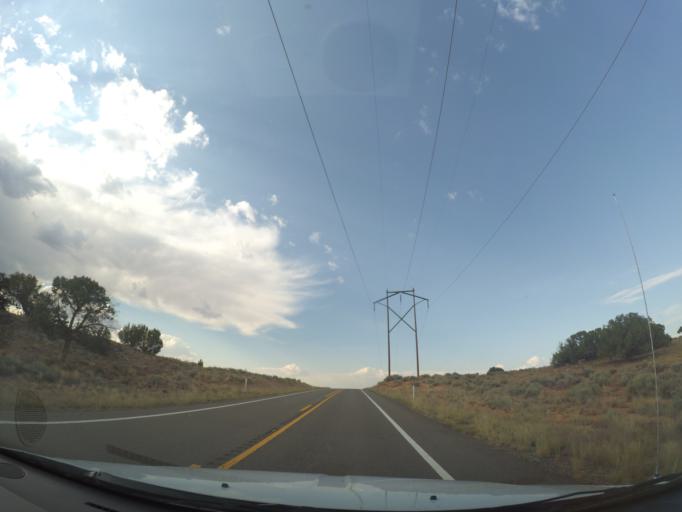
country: US
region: Arizona
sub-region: Coconino County
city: LeChee
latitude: 36.6688
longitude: -111.4410
